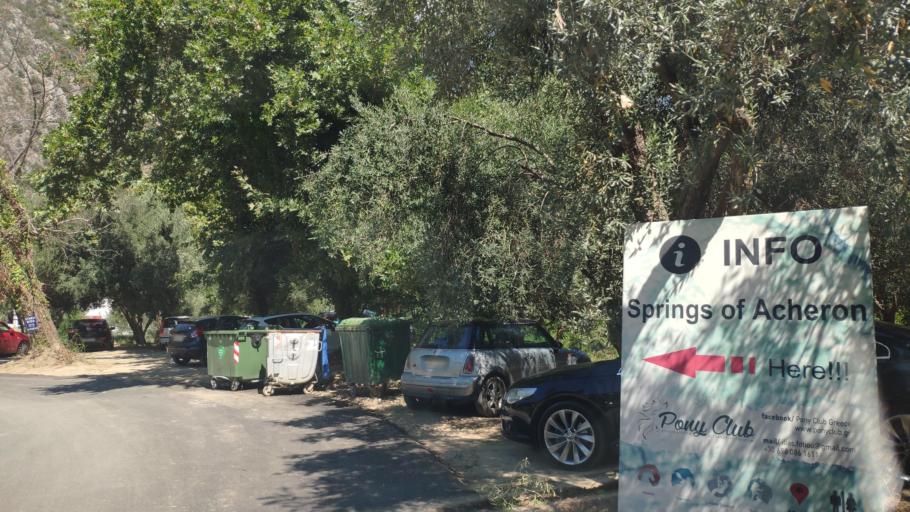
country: GR
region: Epirus
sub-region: Nomos Prevezis
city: Kanalaki
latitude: 39.3268
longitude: 20.6196
